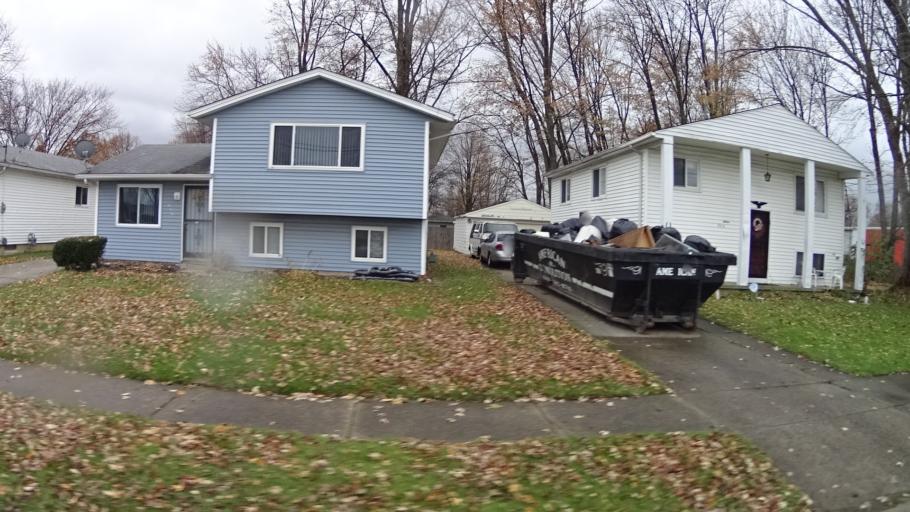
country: US
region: Ohio
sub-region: Lorain County
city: Elyria
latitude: 41.3891
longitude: -82.1233
